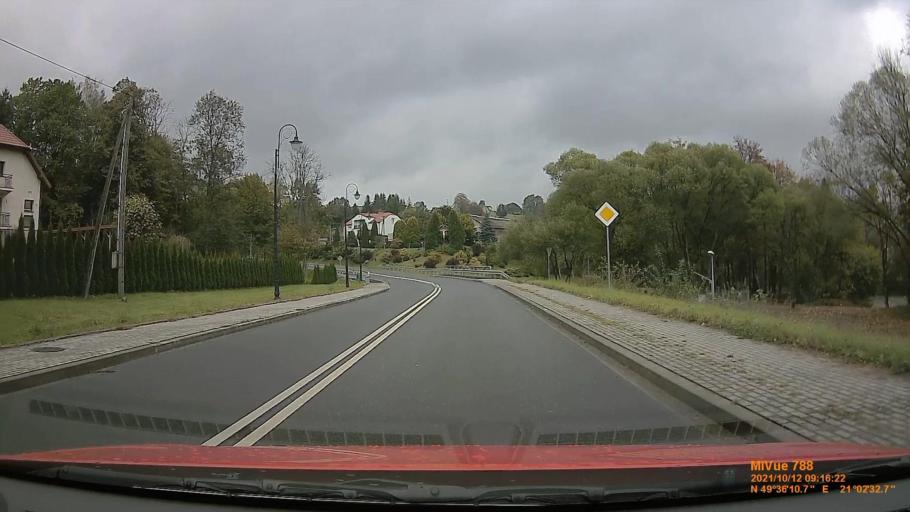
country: PL
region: Lesser Poland Voivodeship
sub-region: Powiat gorlicki
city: Ropa
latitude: 49.6031
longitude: 21.0424
